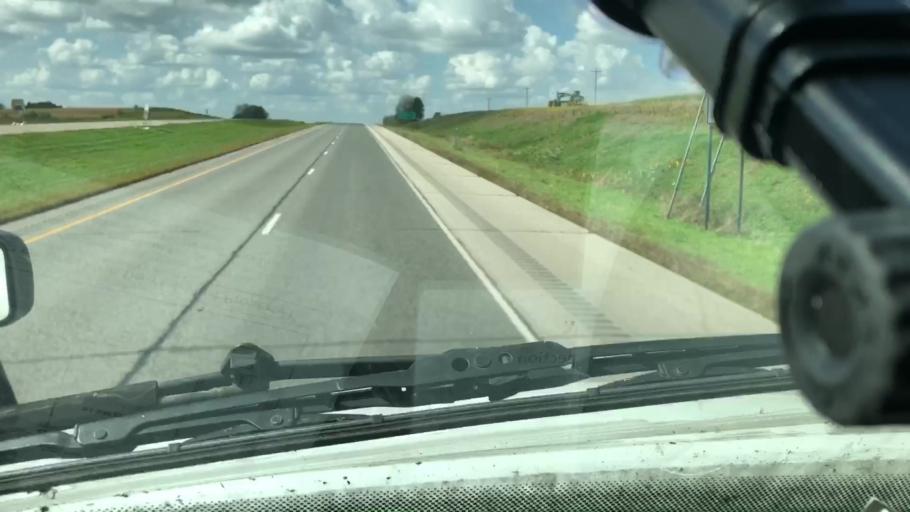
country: US
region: Minnesota
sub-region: Winona County
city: Lewiston
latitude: 43.9335
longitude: -91.8950
